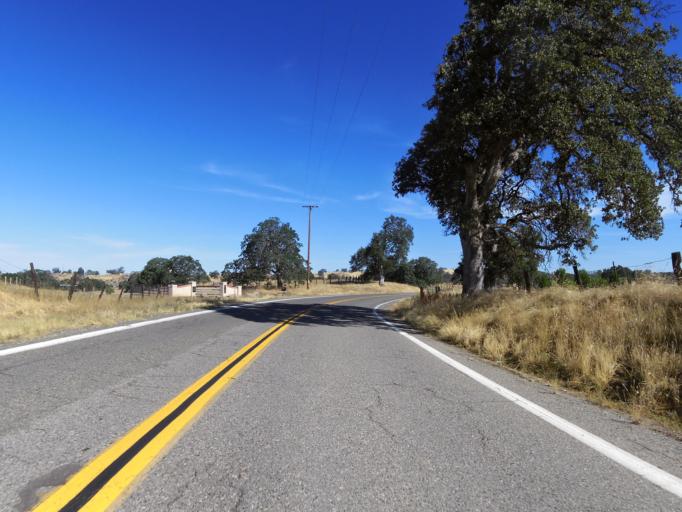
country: US
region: California
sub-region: Madera County
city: Yosemite Lakes
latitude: 37.2007
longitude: -119.9082
